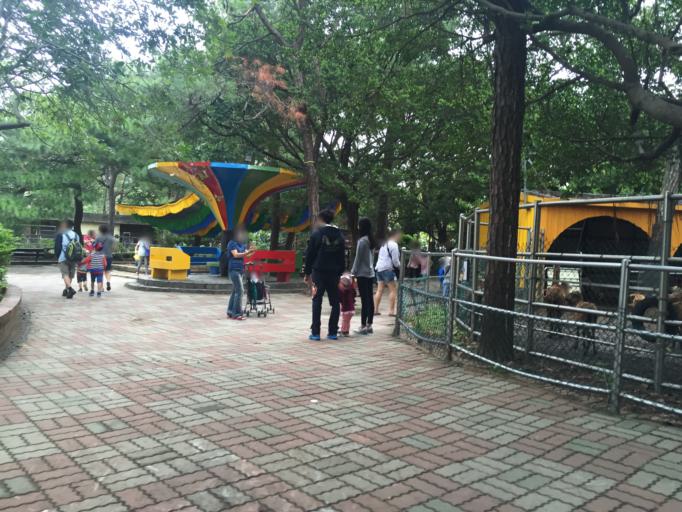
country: TW
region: Taiwan
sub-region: Hsinchu
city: Hsinchu
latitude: 24.8004
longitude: 120.9797
